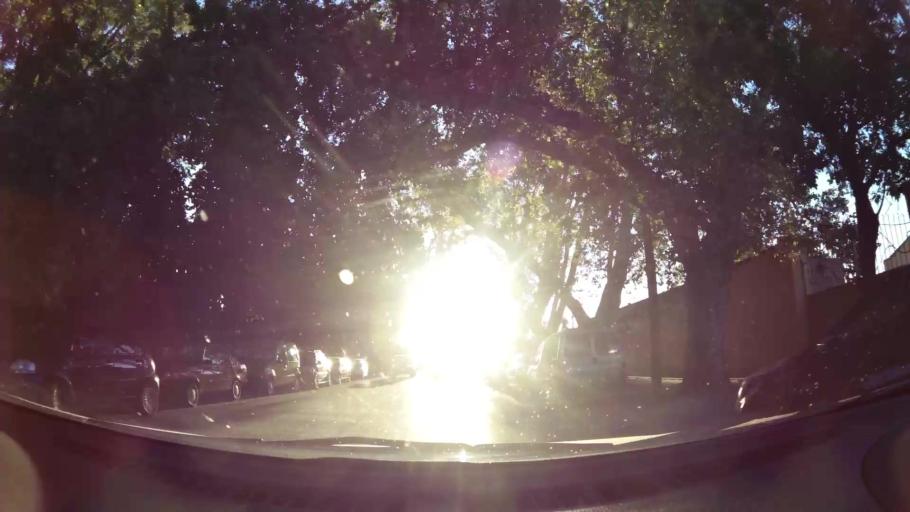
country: AR
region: San Juan
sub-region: Departamento de Santa Lucia
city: Santa Lucia
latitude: -31.5335
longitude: -68.5028
